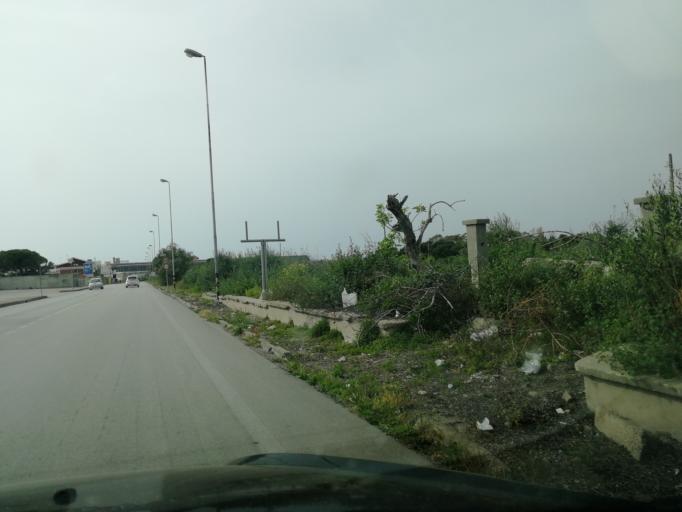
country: IT
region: Apulia
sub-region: Provincia di Barletta - Andria - Trani
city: Barletta
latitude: 41.3136
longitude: 16.3035
